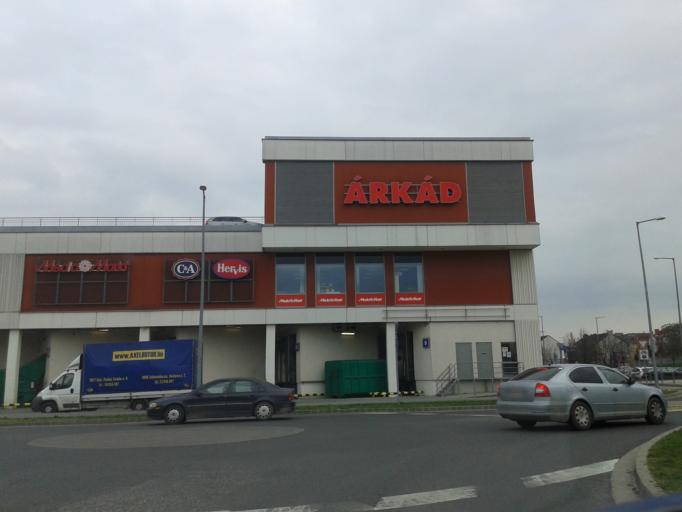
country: HU
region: Gyor-Moson-Sopron
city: Gyor
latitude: 47.6917
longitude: 17.6427
